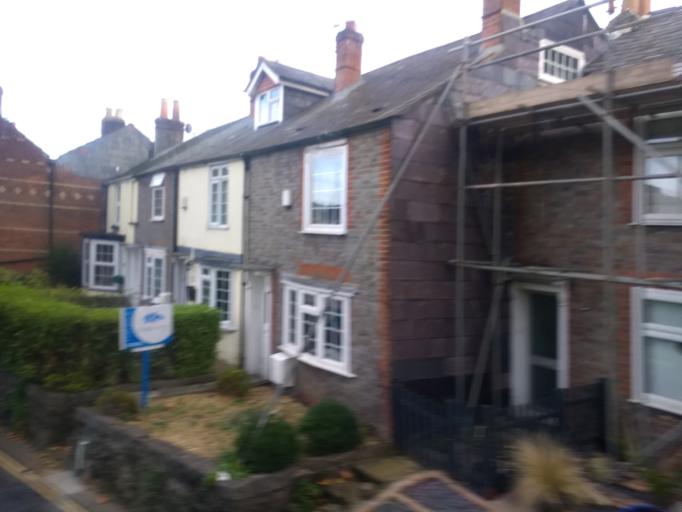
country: GB
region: England
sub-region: Isle of Wight
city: Newport
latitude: 50.6963
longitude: -1.3019
